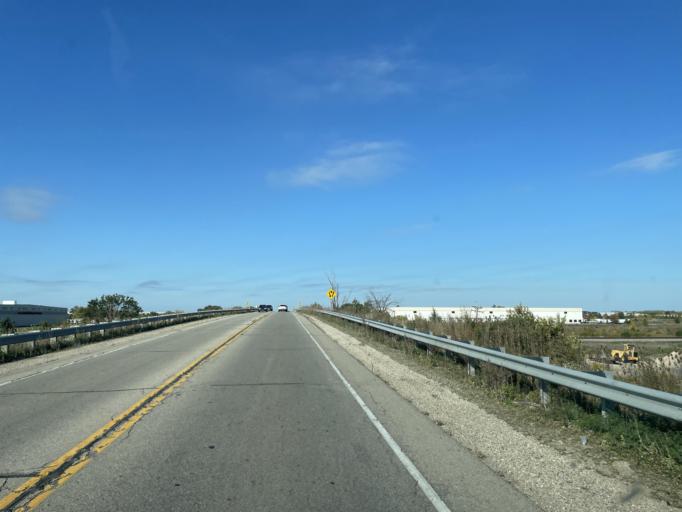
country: US
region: Wisconsin
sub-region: Kenosha County
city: Pleasant Prairie
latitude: 42.5889
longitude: -87.9031
